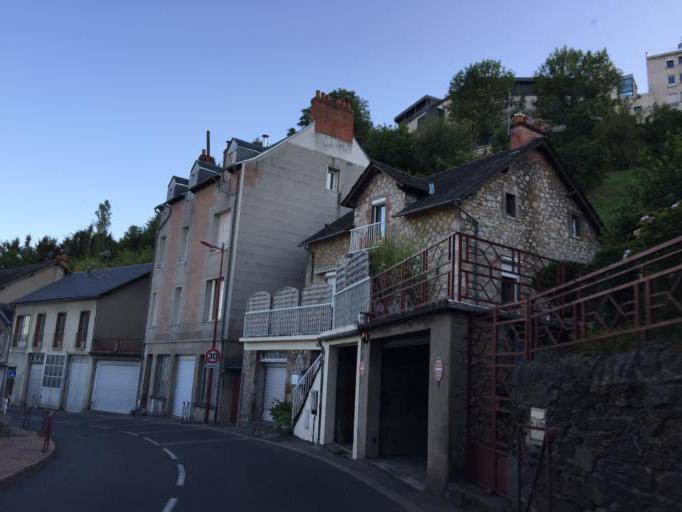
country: FR
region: Midi-Pyrenees
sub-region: Departement de l'Aveyron
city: Rodez
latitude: 44.3540
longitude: 2.5784
